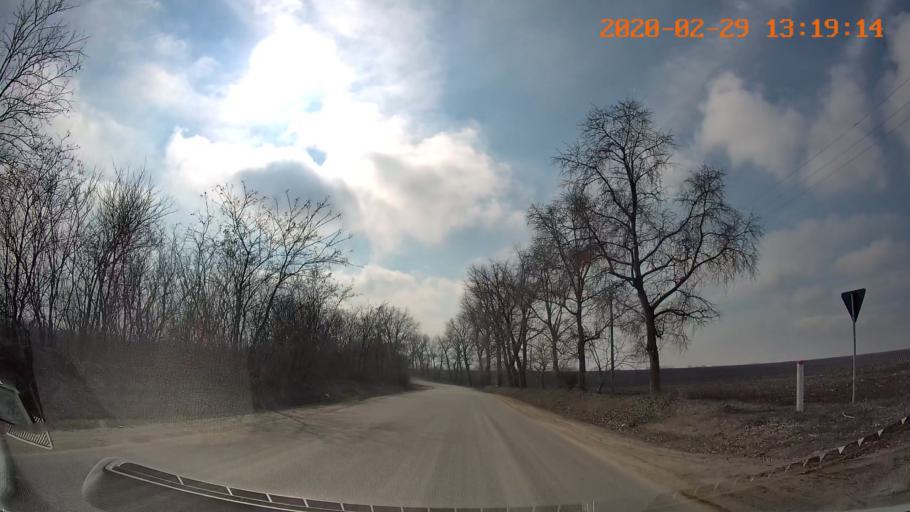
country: MD
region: Telenesti
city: Camenca
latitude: 47.9904
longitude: 28.6528
